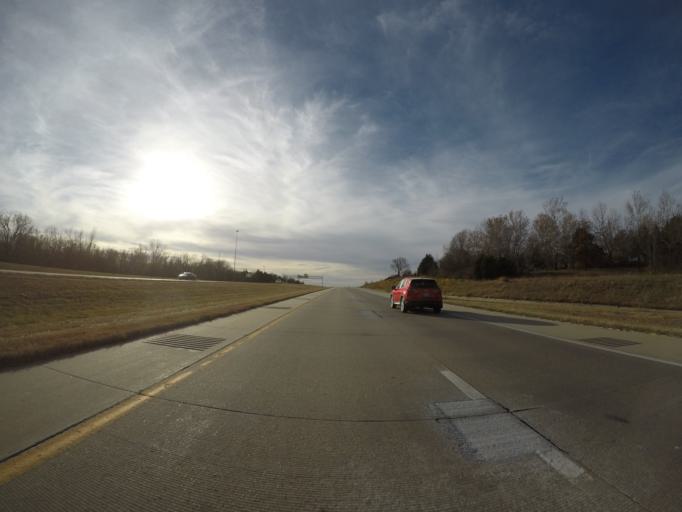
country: US
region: Kansas
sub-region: Franklin County
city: Ottawa
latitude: 38.5701
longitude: -95.2882
